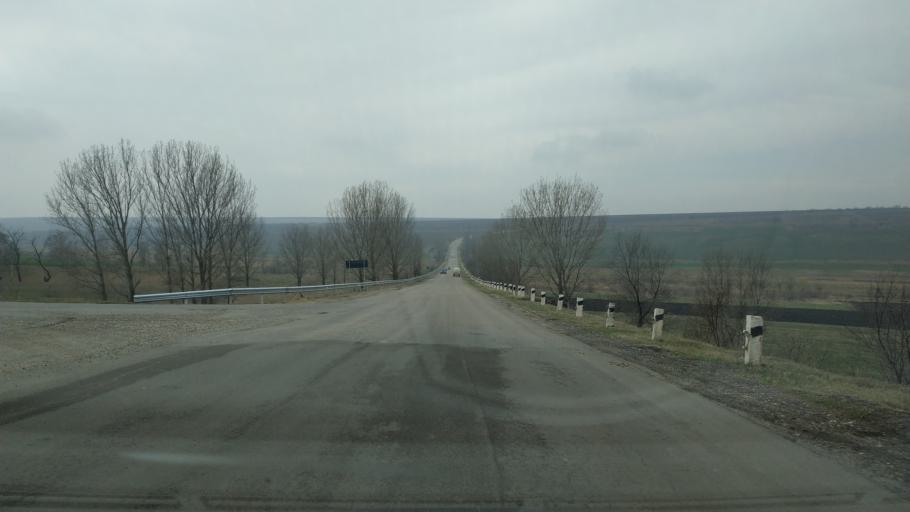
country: MD
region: Cahul
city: Cahul
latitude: 45.9586
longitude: 28.4095
